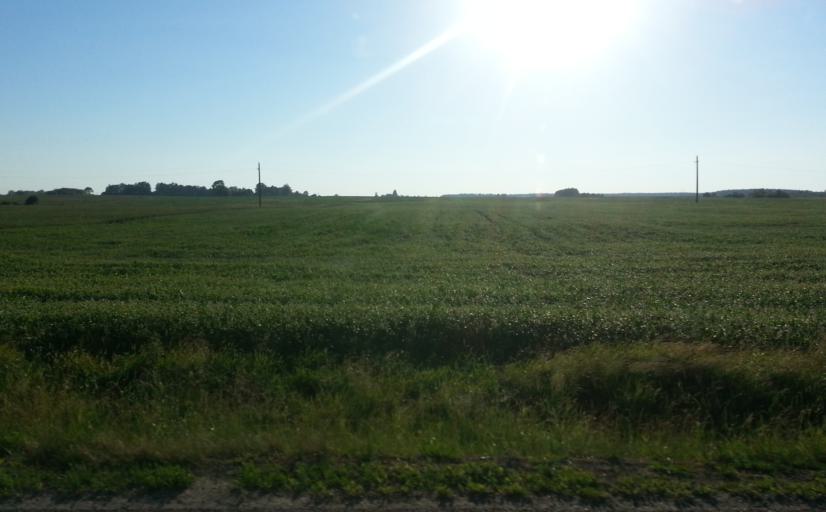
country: LT
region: Panevezys
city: Pasvalys
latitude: 55.9413
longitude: 24.3371
